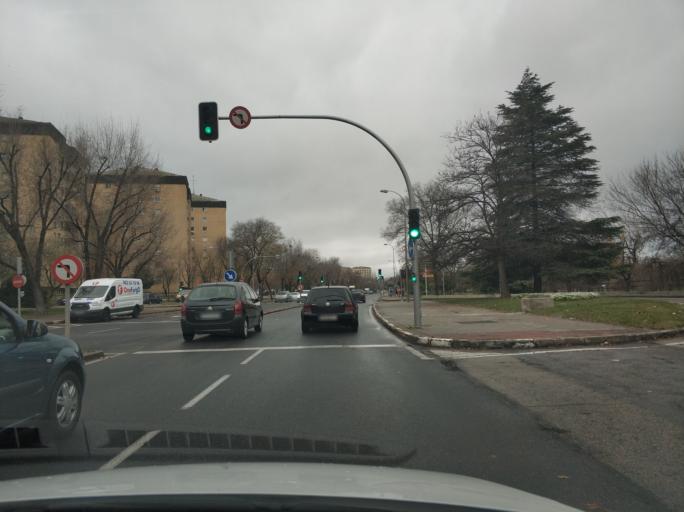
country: ES
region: Madrid
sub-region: Provincia de Madrid
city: Usera
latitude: 40.3713
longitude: -3.7042
